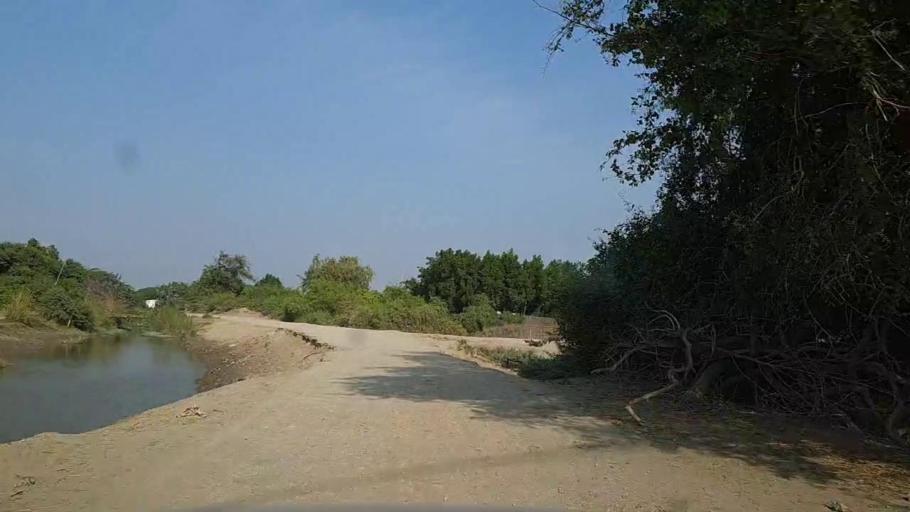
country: PK
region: Sindh
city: Mirpur Sakro
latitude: 24.5916
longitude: 67.5747
